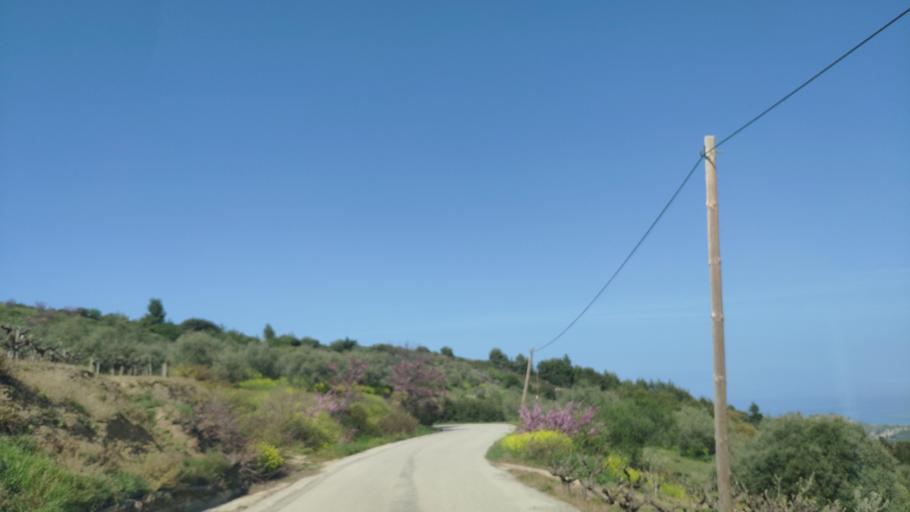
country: GR
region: West Greece
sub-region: Nomos Achaias
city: Akrata
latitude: 38.1113
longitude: 22.3203
